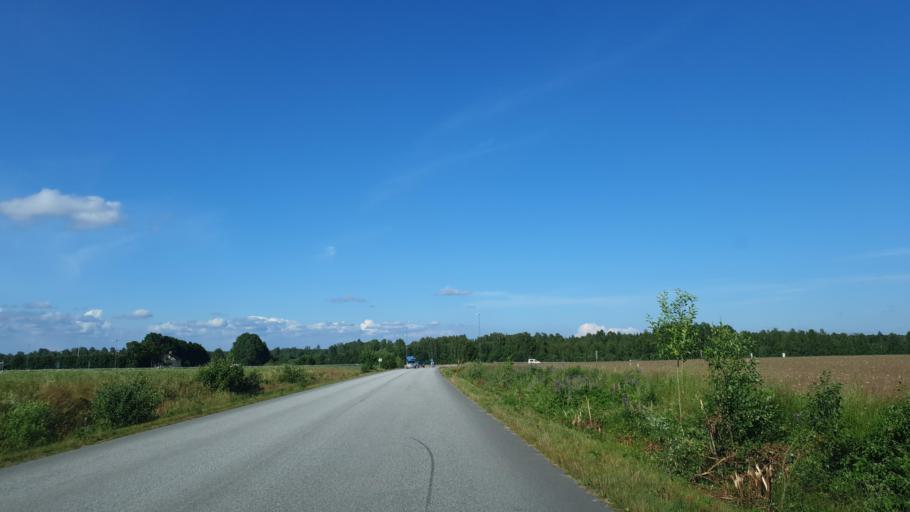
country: SE
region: Dalarna
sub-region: Avesta Kommun
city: Avesta
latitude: 60.1267
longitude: 16.2743
